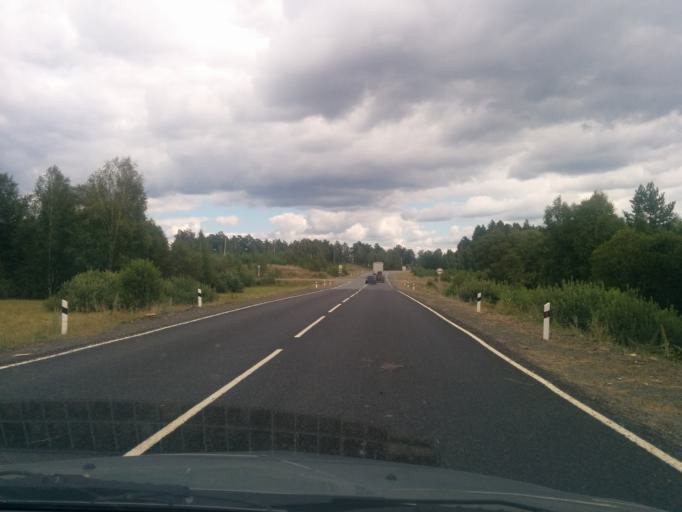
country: RU
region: Bashkortostan
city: Lomovka
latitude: 53.8969
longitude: 58.0856
